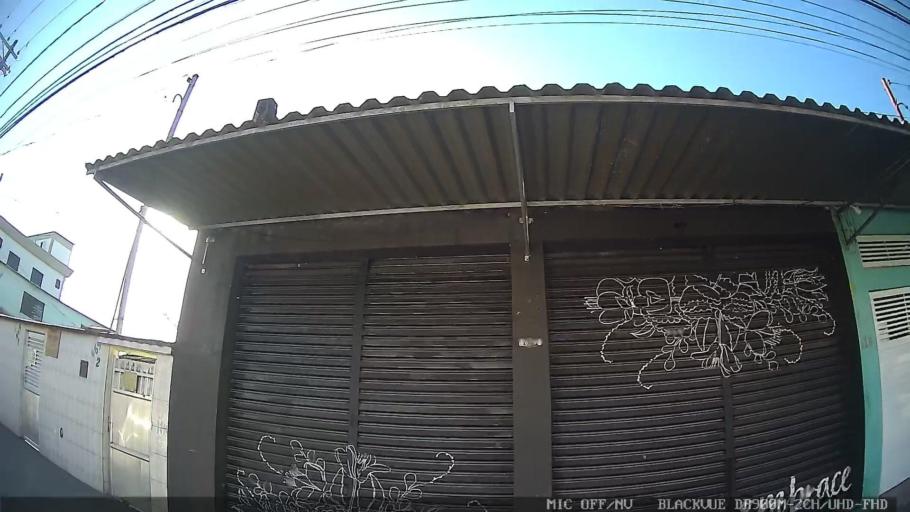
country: BR
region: Sao Paulo
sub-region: Santos
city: Santos
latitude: -23.9598
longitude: -46.2938
